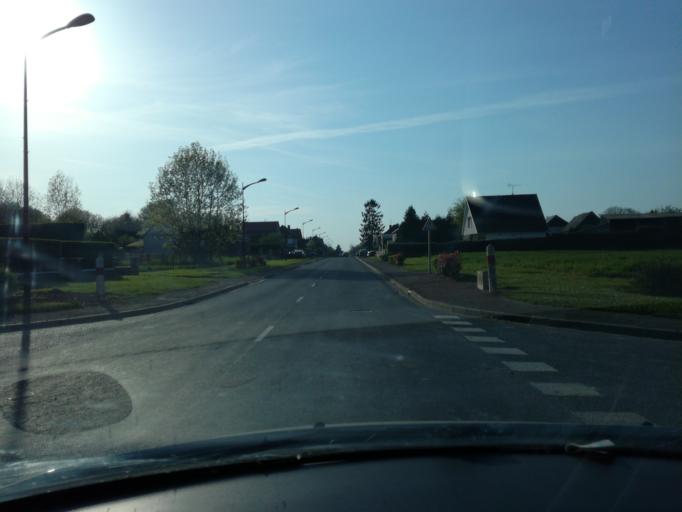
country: FR
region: Picardie
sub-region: Departement de la Somme
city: Hornoy-le-Bourg
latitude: 49.8250
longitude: 1.9453
